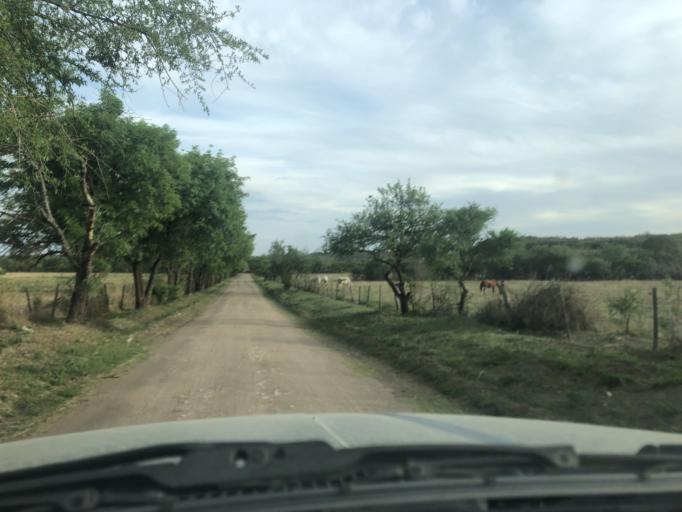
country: AR
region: Cordoba
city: La Granja
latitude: -31.0145
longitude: -64.2521
